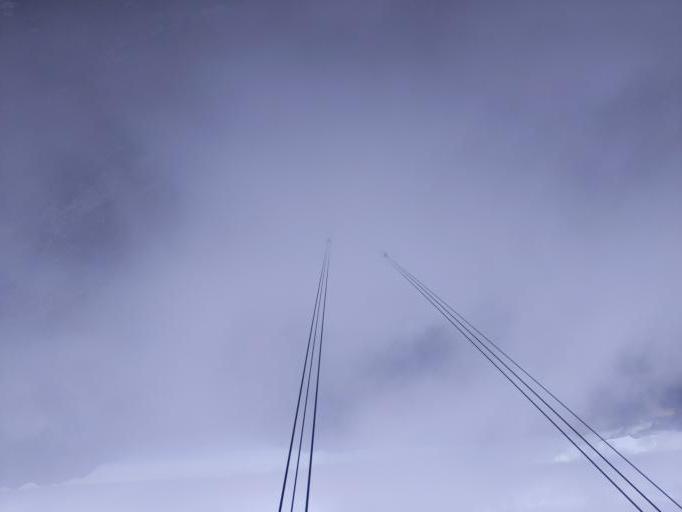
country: DE
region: Bavaria
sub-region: Upper Bavaria
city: Grainau
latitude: 47.4402
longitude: 11.0514
